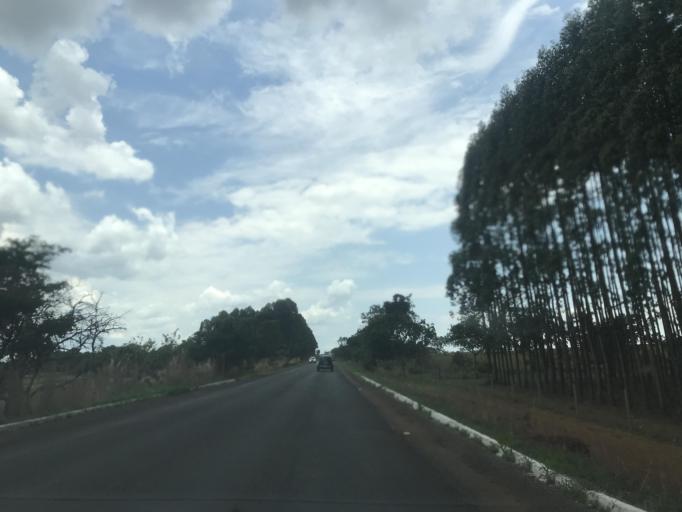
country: BR
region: Goias
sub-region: Vianopolis
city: Vianopolis
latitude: -16.9344
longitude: -48.5575
